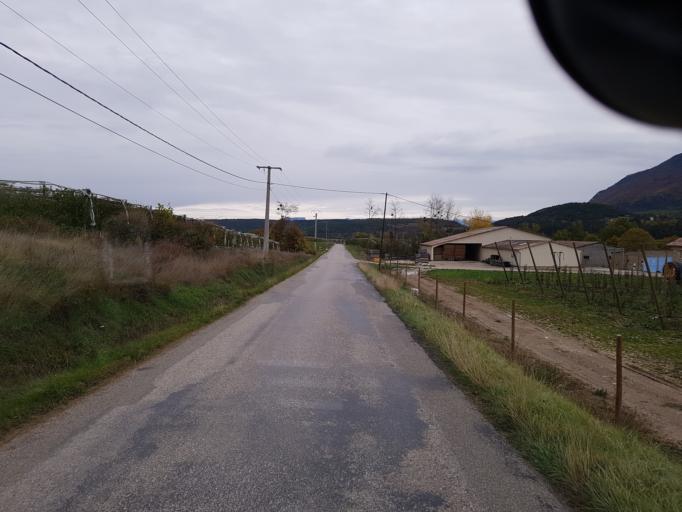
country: FR
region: Provence-Alpes-Cote d'Azur
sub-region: Departement des Hautes-Alpes
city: Laragne-Monteglin
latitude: 44.3201
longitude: 5.7281
